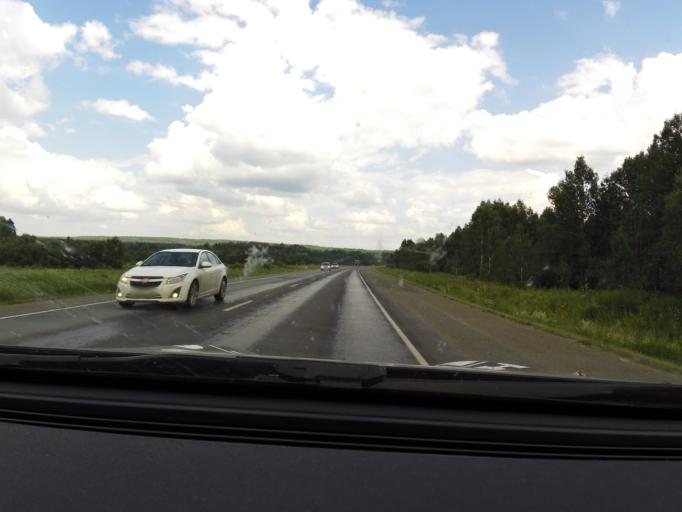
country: RU
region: Sverdlovsk
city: Bisert'
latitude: 56.8349
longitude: 58.9101
